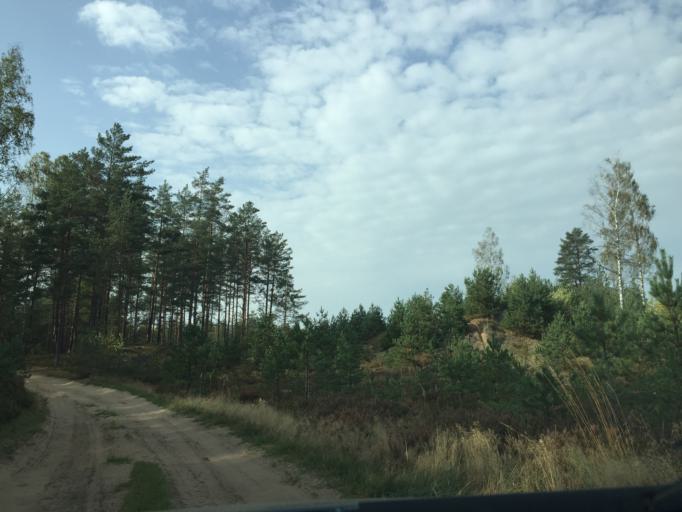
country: LV
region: Garkalne
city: Garkalne
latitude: 56.9556
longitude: 24.4192
